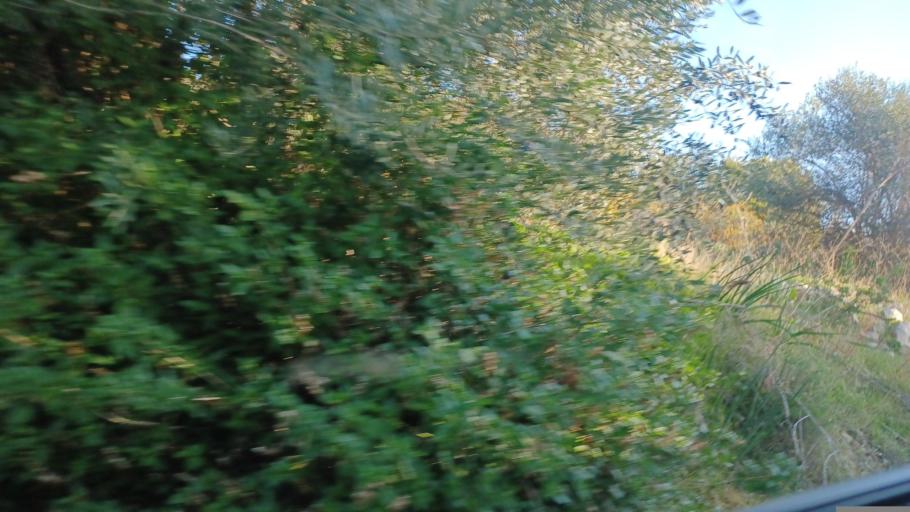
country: CY
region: Pafos
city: Mesogi
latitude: 34.8687
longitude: 32.5746
